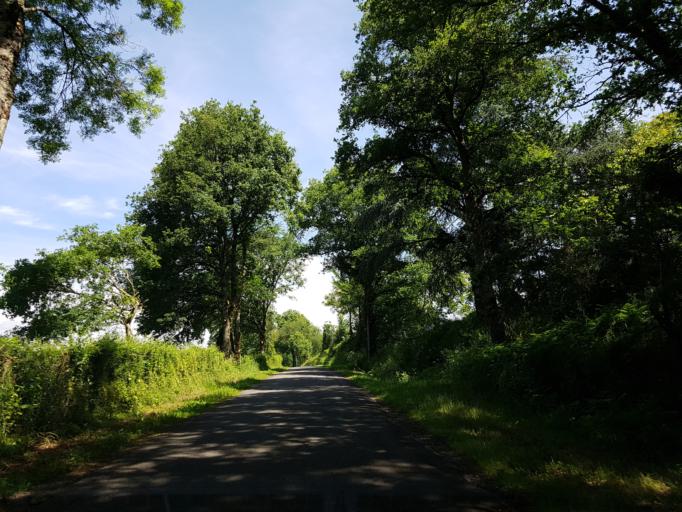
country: FR
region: Poitou-Charentes
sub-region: Departement de la Charente
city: Chabanais
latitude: 45.8893
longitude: 0.7418
